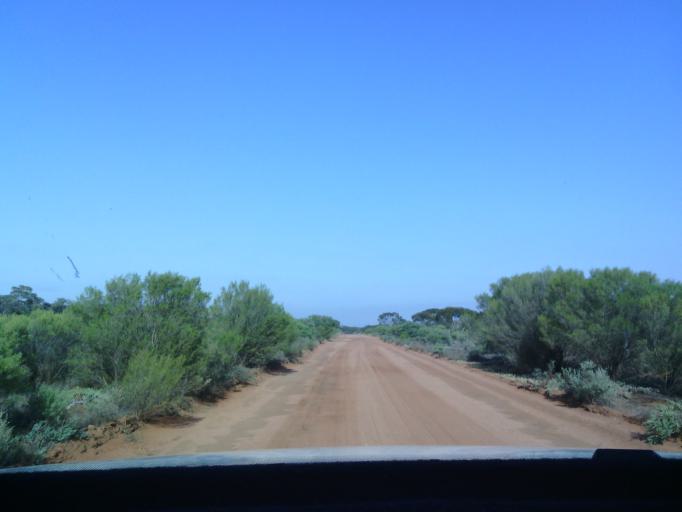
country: AU
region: South Australia
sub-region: Berri and Barmera
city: Monash
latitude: -34.2250
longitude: 140.5862
